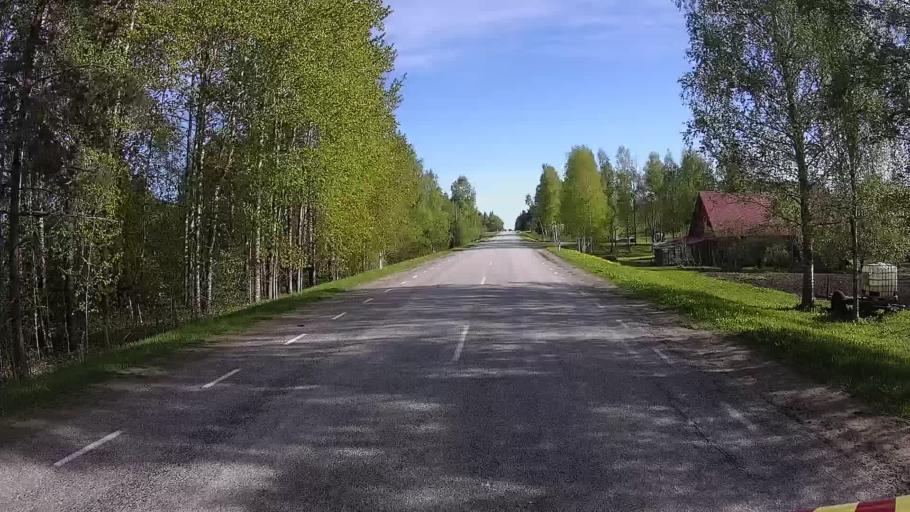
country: EE
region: Tartu
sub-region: Elva linn
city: Elva
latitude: 58.1396
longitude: 26.5210
